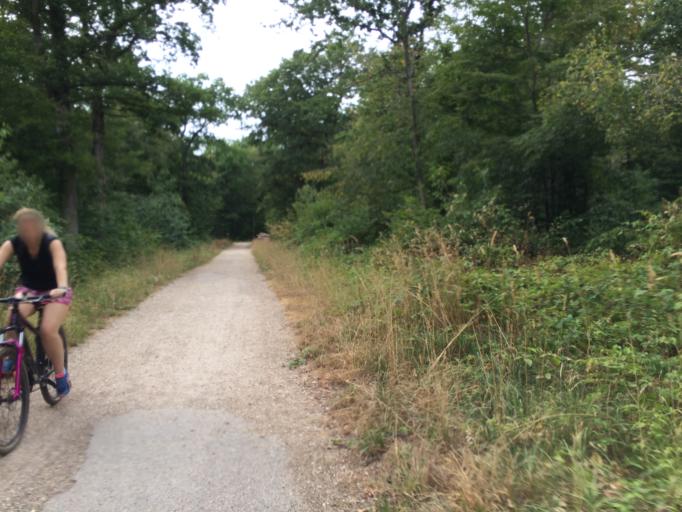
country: FR
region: Ile-de-France
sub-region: Departement de l'Essonne
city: Quincy-sous-Senart
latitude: 48.6601
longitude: 2.5418
